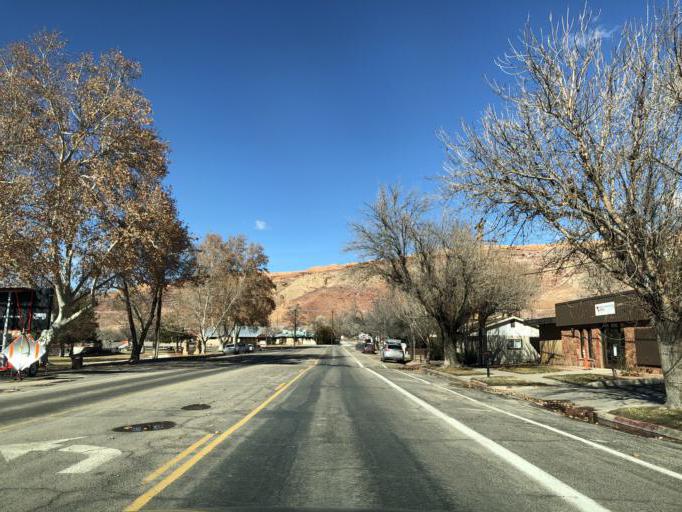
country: US
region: Utah
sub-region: Grand County
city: Moab
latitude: 38.5778
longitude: -109.5527
